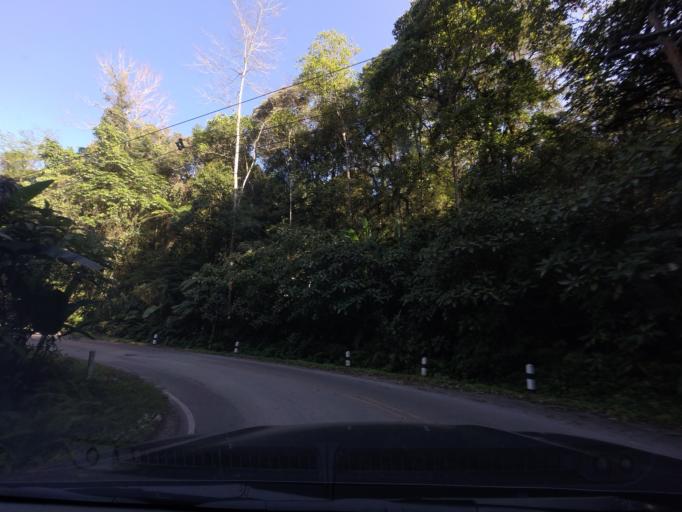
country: TH
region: Phetchabun
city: Lom Kao
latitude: 16.8988
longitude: 101.0850
